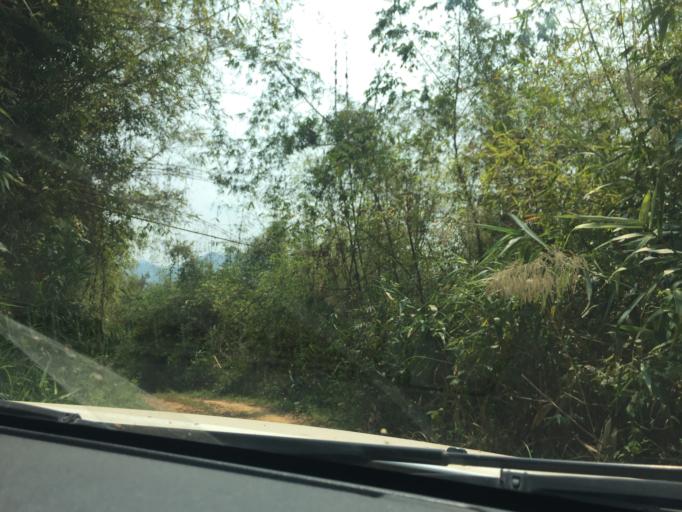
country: LA
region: Loungnamtha
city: Muang Nale
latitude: 20.6126
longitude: 101.6015
